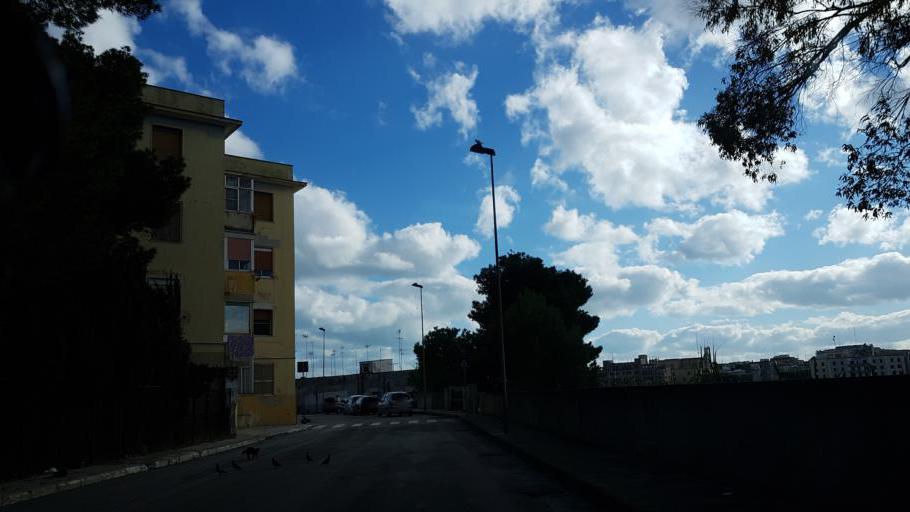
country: IT
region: Apulia
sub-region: Provincia di Brindisi
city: Brindisi
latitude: 40.6438
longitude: 17.9390
